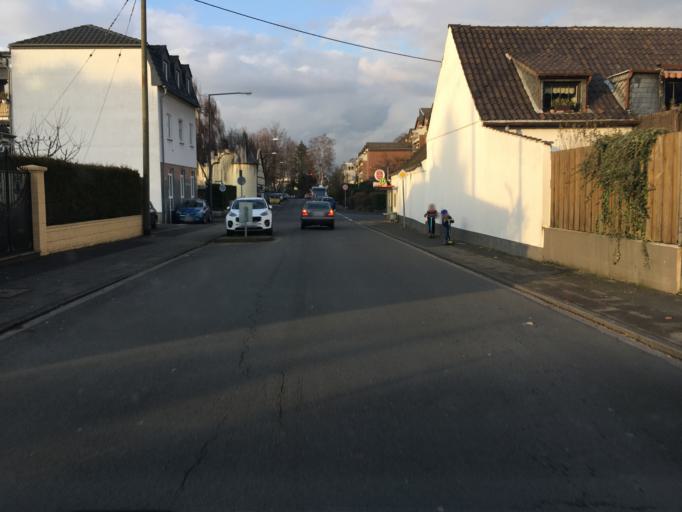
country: DE
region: North Rhine-Westphalia
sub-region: Regierungsbezirk Koln
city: Frechen
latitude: 50.9346
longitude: 6.8268
